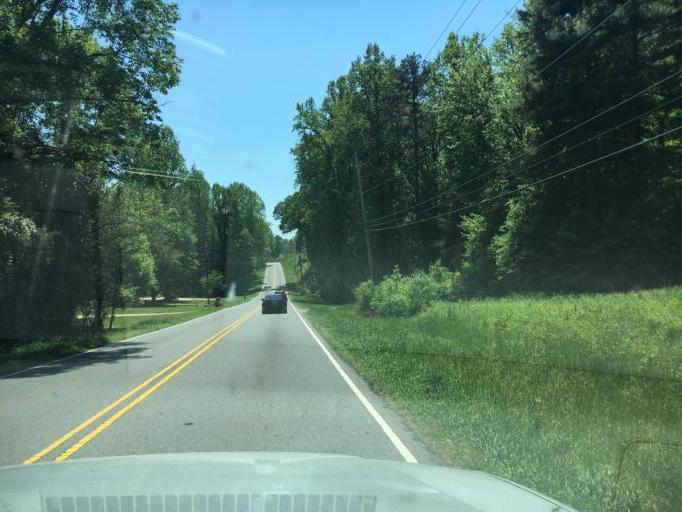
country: US
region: North Carolina
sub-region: Cleveland County
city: Shelby
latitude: 35.2494
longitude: -81.5664
